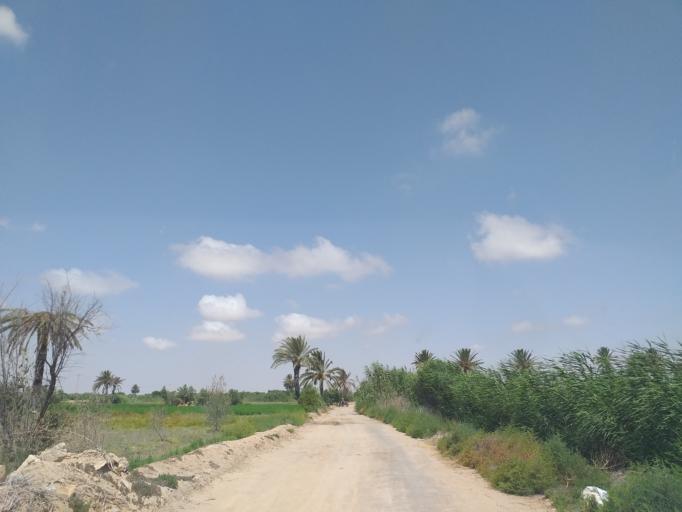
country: TN
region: Qabis
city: Gabes
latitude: 33.9525
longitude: 10.0480
